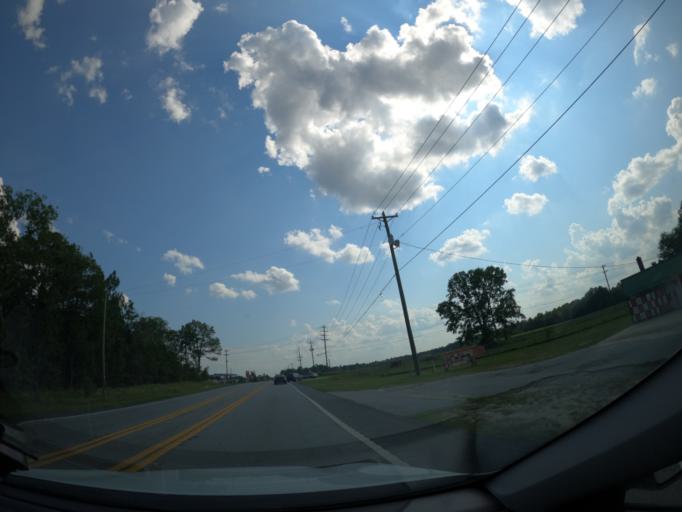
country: US
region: South Carolina
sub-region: Lexington County
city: Gaston
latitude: 33.7824
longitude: -81.2368
